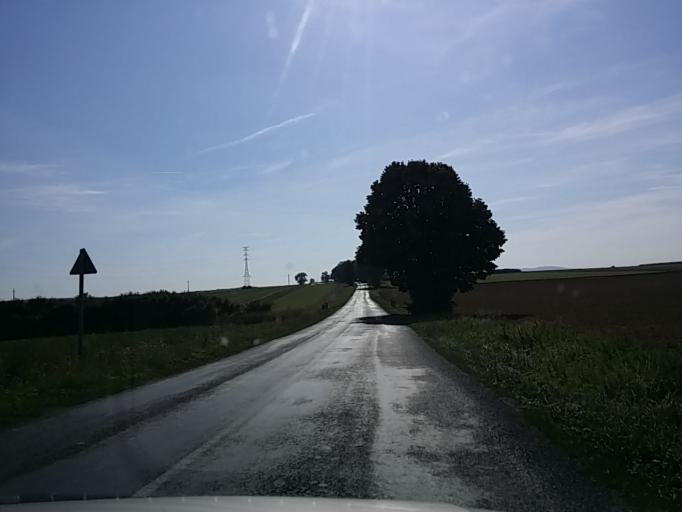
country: AT
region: Burgenland
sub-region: Politischer Bezirk Oberpullendorf
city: Lutzmannsburg
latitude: 47.4366
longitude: 16.6647
